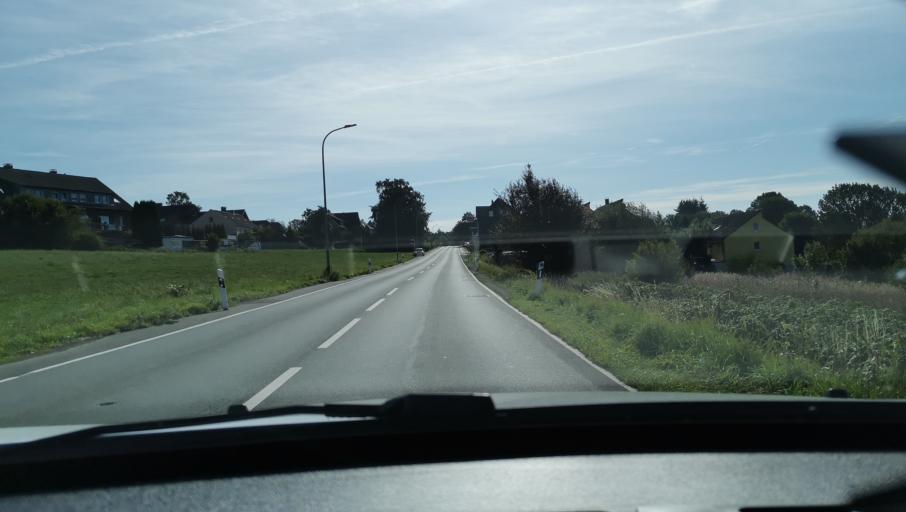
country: DE
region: North Rhine-Westphalia
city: Ennepetal
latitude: 51.2917
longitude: 7.4177
